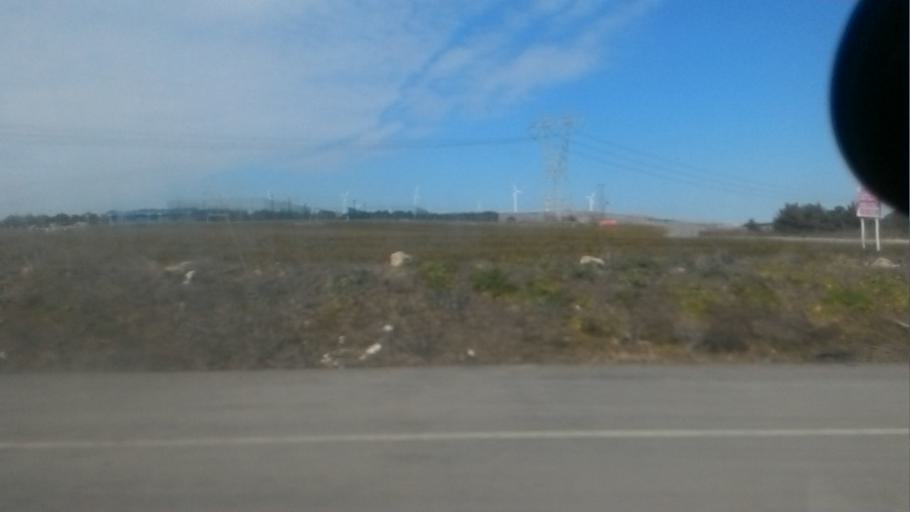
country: TR
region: Istanbul
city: Canta
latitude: 41.0811
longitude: 28.0543
